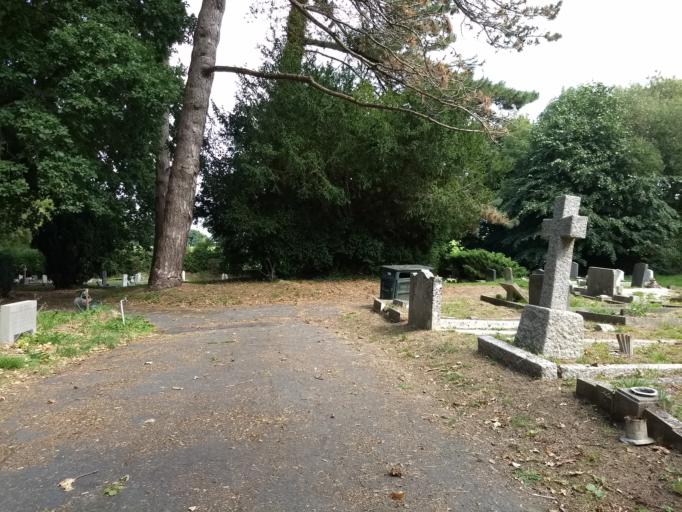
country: GB
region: England
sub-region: Isle of Wight
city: Newport
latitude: 50.7078
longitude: -1.2818
